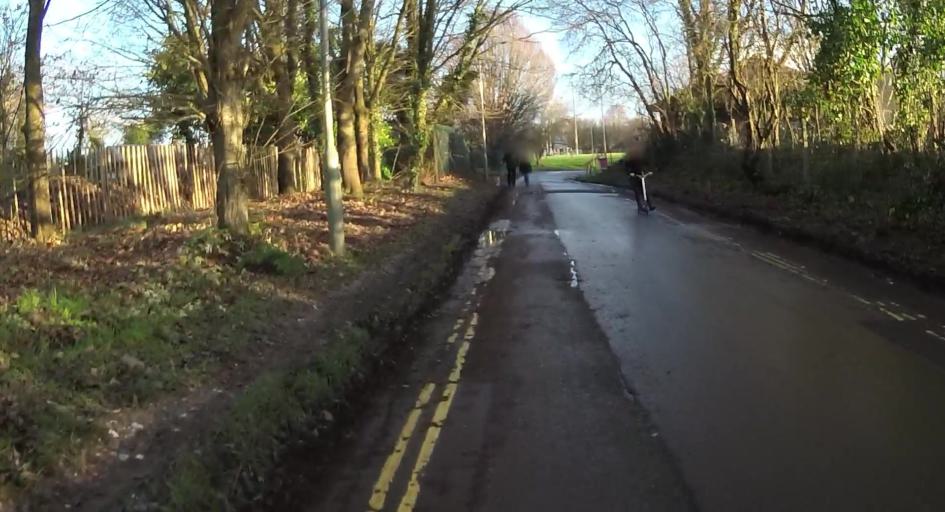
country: GB
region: England
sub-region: Hampshire
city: Winchester
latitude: 51.0724
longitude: -1.3094
